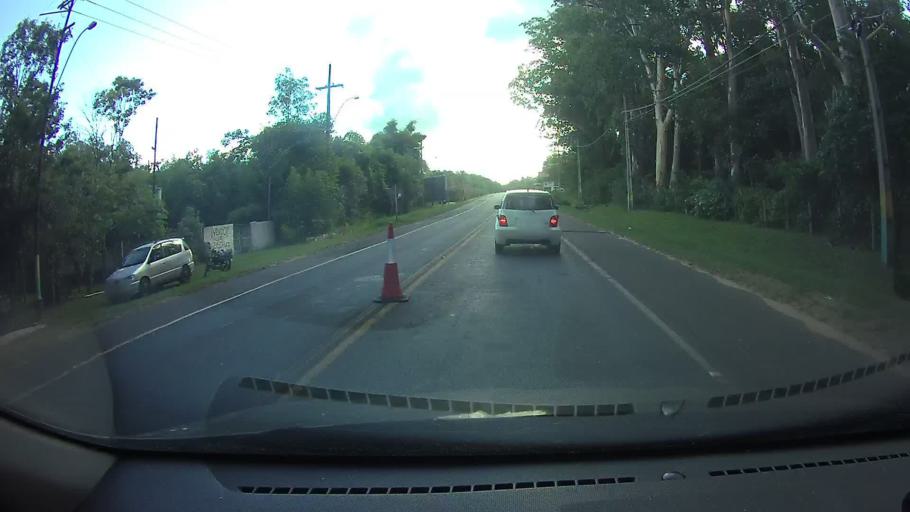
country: PY
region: Cordillera
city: Caacupe
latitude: -25.3899
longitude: -57.0668
